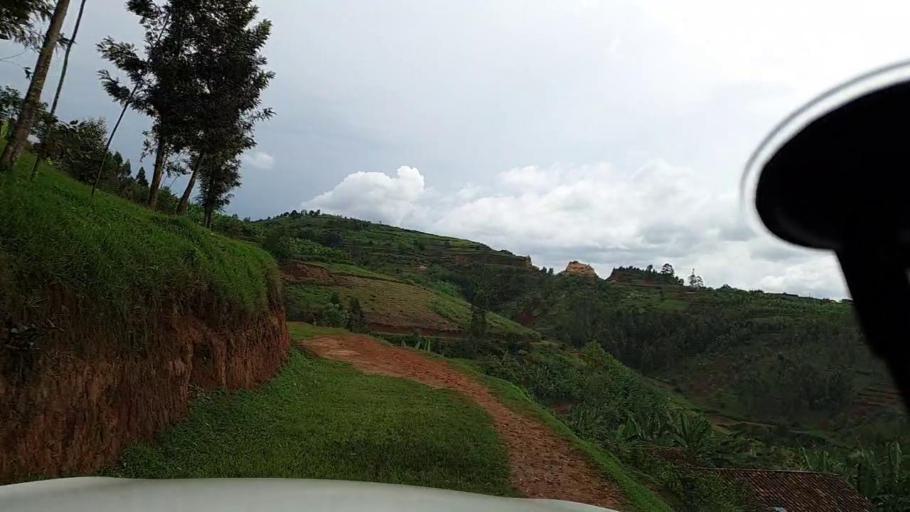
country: RW
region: Southern Province
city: Gitarama
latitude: -2.0787
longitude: 29.6433
